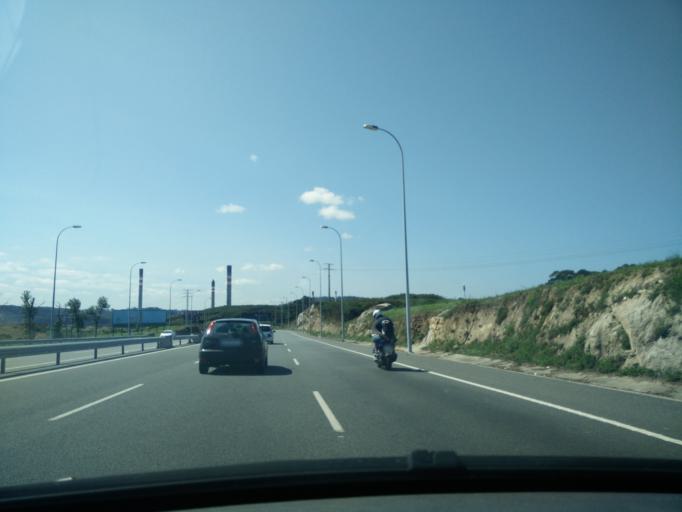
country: ES
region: Galicia
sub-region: Provincia da Coruna
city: A Coruna
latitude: 43.3578
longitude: -8.4347
